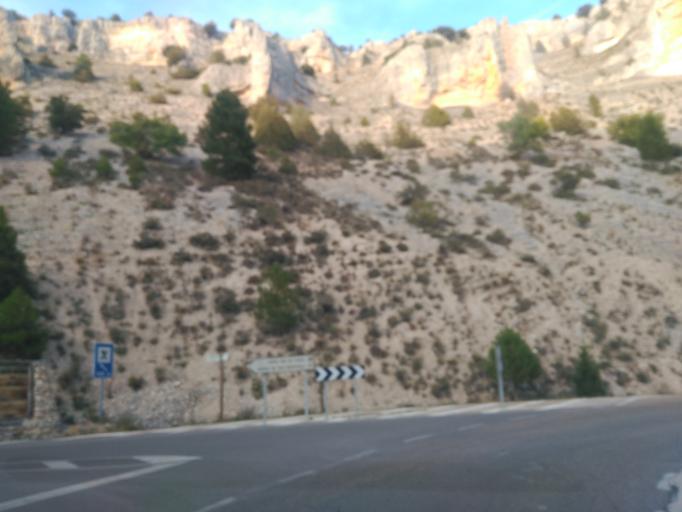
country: ES
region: Castille and Leon
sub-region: Provincia de Soria
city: Ucero
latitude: 41.7330
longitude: -3.0457
